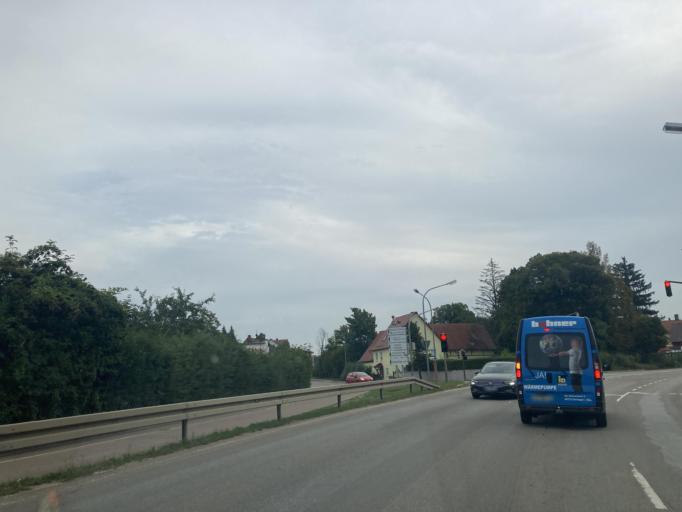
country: DE
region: Bavaria
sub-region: Swabia
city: Oettingen in Bayern
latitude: 48.9473
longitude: 10.5986
